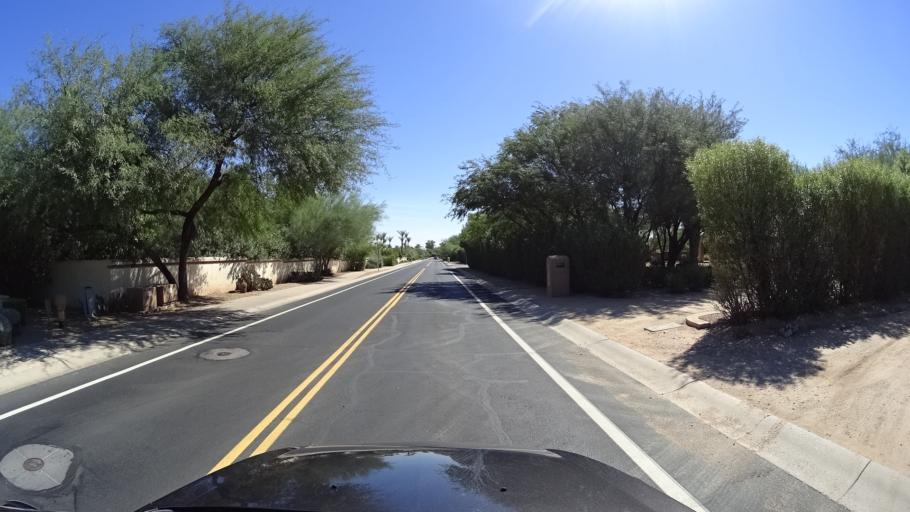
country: US
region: Arizona
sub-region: Maricopa County
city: Paradise Valley
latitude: 33.5459
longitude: -111.9327
